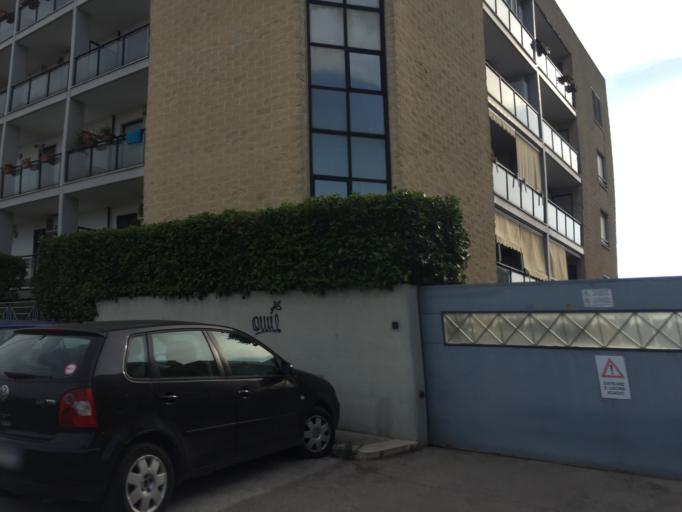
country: IT
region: Apulia
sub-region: Provincia di Bari
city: Capurso
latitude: 41.0514
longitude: 16.9217
